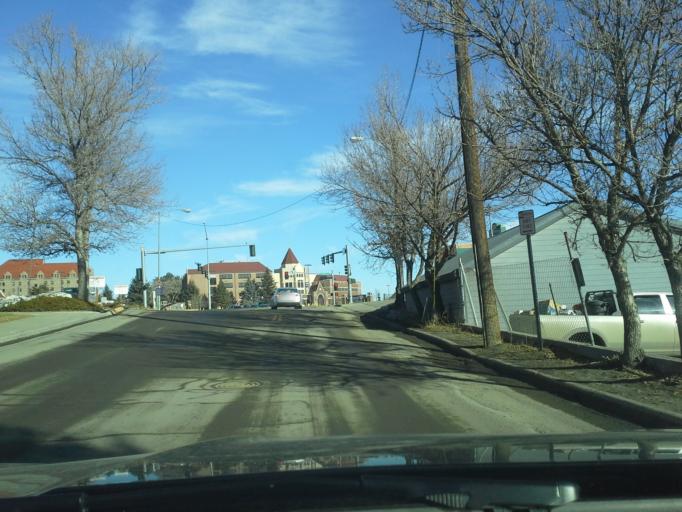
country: US
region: Montana
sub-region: Lewis and Clark County
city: Helena
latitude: 46.5973
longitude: -112.0379
